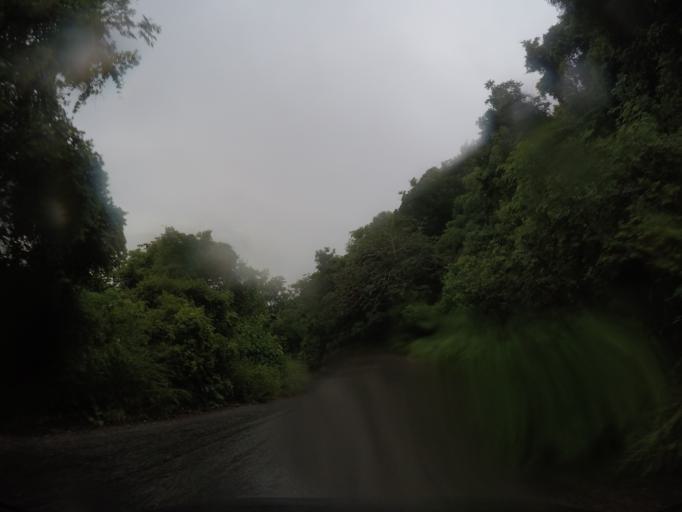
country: MX
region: Oaxaca
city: San Gabriel Mixtepec
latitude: 16.0577
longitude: -97.0768
